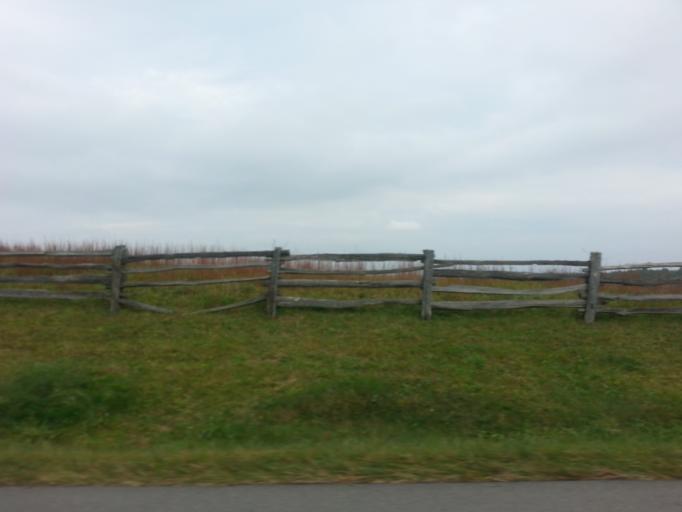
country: US
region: North Carolina
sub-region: Ashe County
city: Jefferson
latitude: 36.3433
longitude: -81.3749
